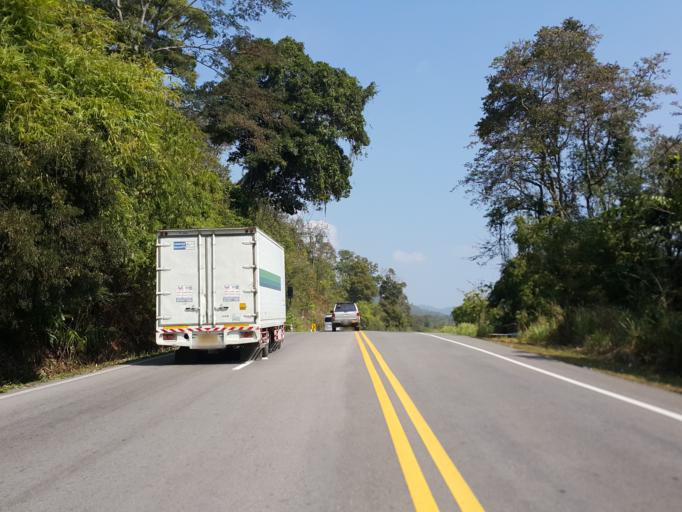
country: TH
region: Chiang Mai
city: Mae On
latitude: 19.0086
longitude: 99.2915
